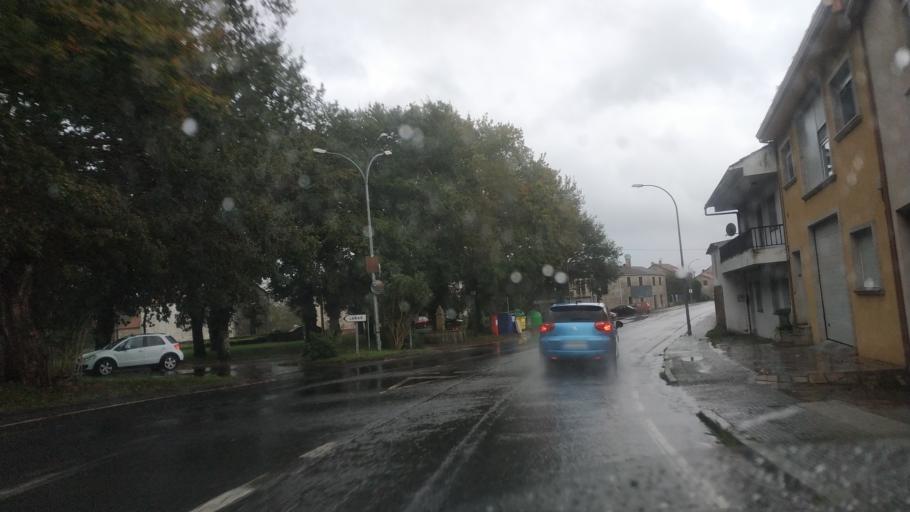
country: ES
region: Galicia
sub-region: Provincia da Coruna
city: Negreira
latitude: 42.9245
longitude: -8.7341
